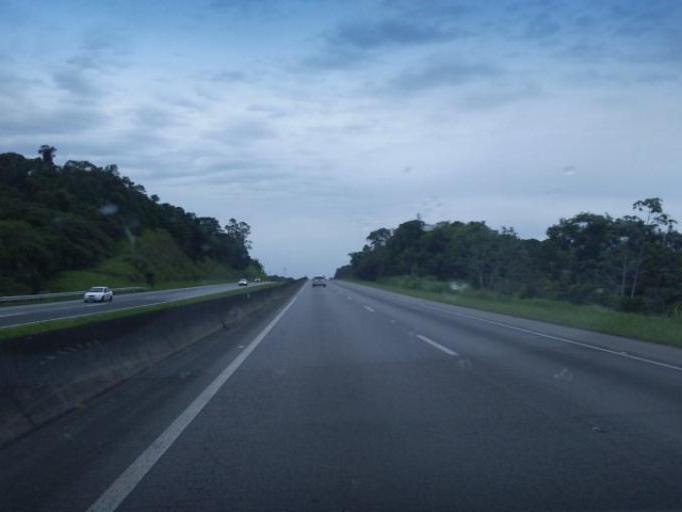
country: BR
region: Sao Paulo
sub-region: Registro
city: Registro
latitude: -24.4392
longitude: -47.7961
